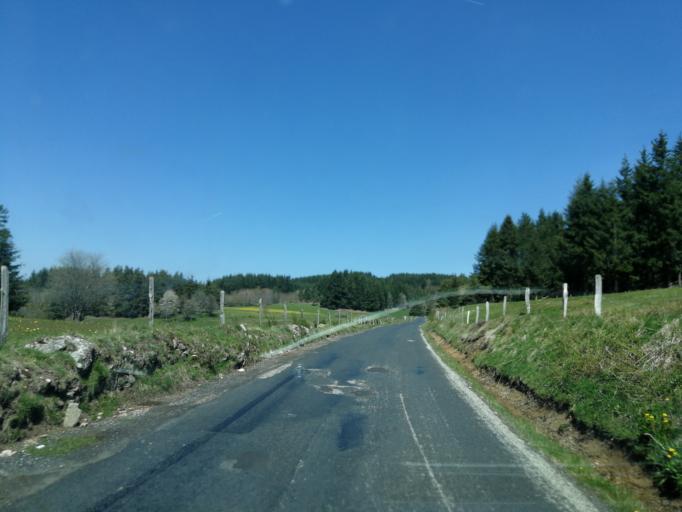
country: FR
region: Rhone-Alpes
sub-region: Departement de l'Ardeche
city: Le Cheylard
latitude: 44.9454
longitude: 4.4193
